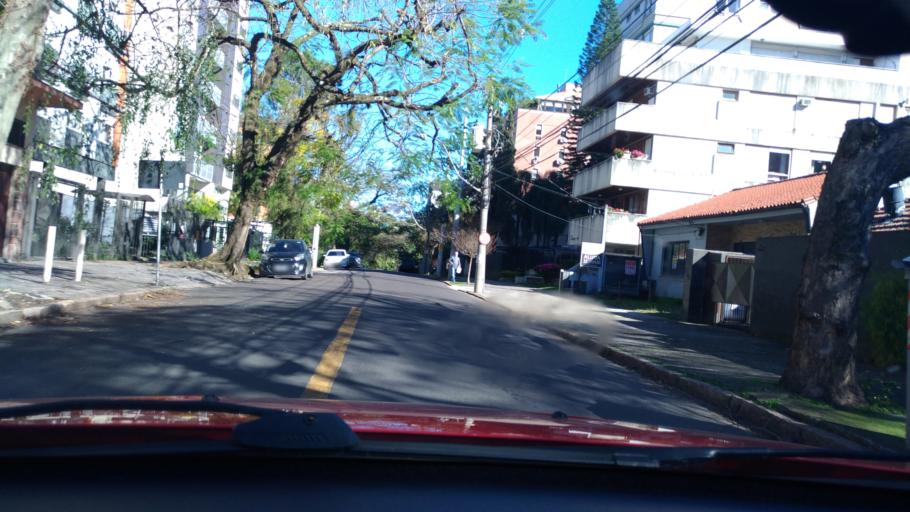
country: BR
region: Rio Grande do Sul
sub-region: Porto Alegre
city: Porto Alegre
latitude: -30.0177
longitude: -51.1876
